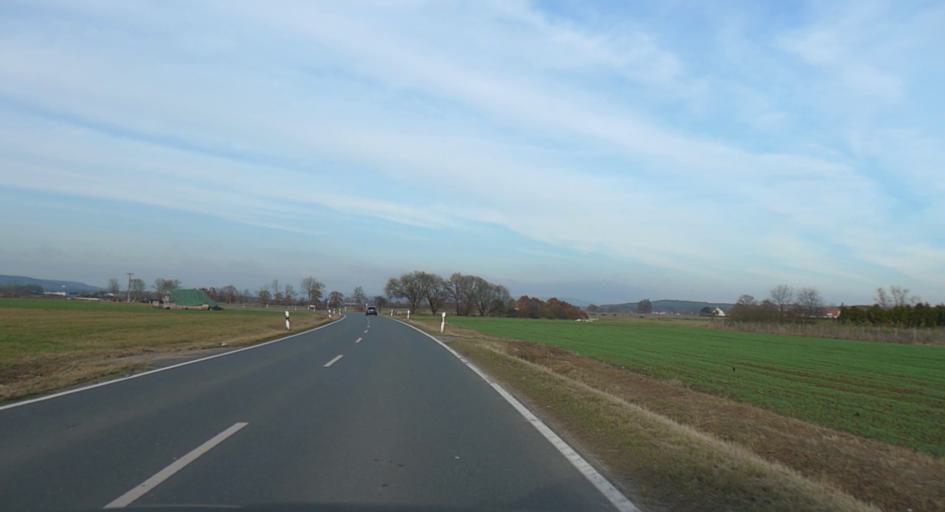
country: DE
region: Bavaria
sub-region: Regierungsbezirk Mittelfranken
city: Baiersdorf
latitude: 49.6513
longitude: 11.0467
